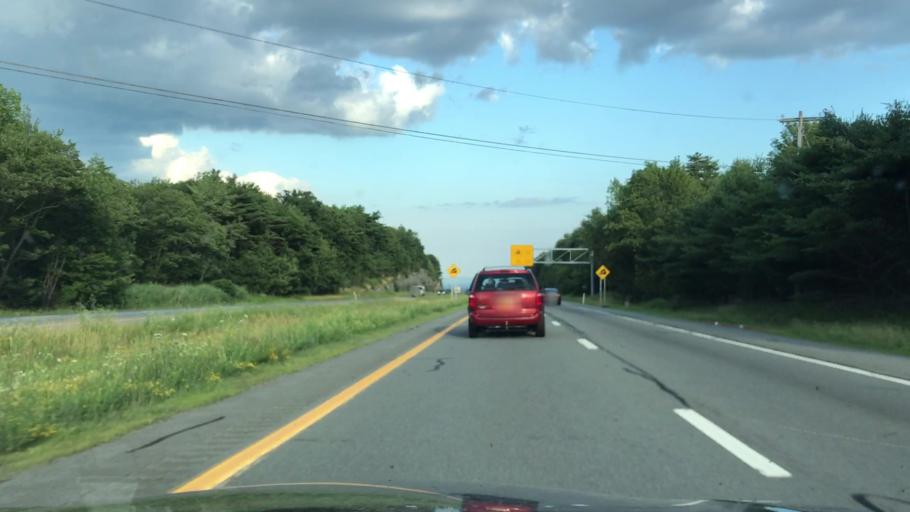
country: US
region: New York
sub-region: Sullivan County
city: Rock Hill
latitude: 41.5973
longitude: -74.5442
